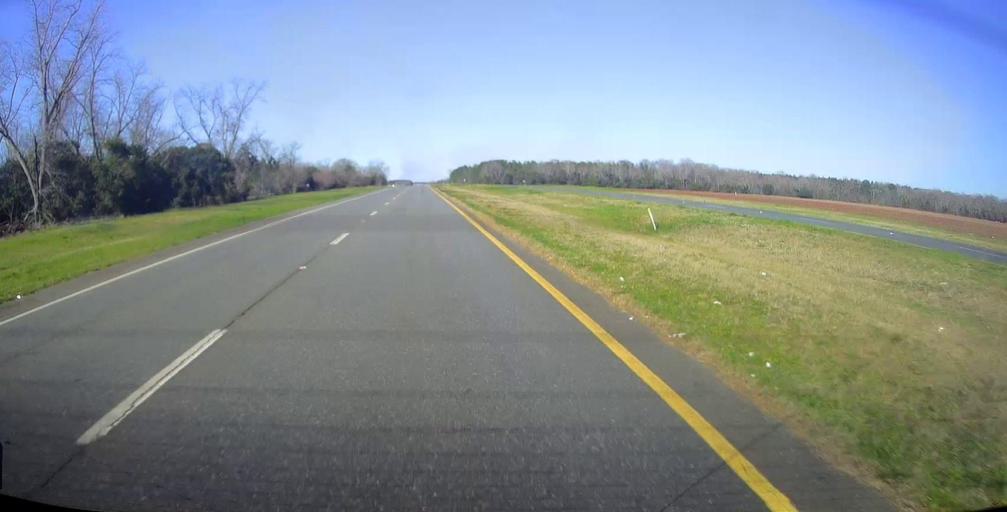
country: US
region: Georgia
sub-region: Schley County
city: Ellaville
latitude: 32.1752
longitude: -84.2685
